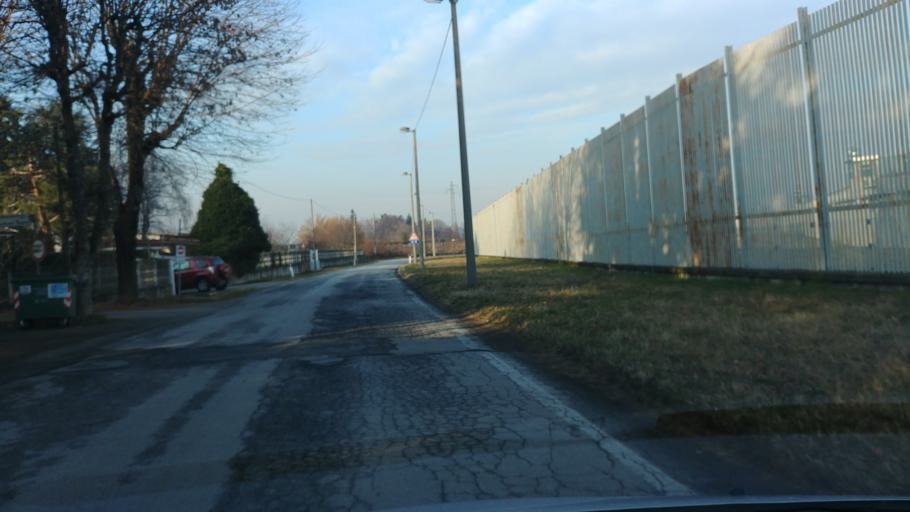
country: IT
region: Piedmont
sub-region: Provincia di Cuneo
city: Cuneo
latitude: 44.4040
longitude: 7.5361
